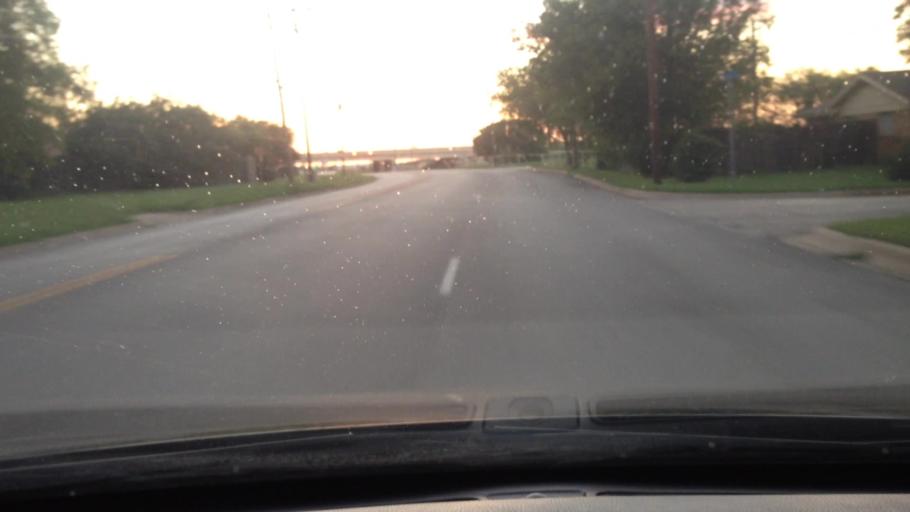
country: US
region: Texas
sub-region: Tarrant County
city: White Settlement
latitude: 32.7742
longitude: -97.4720
